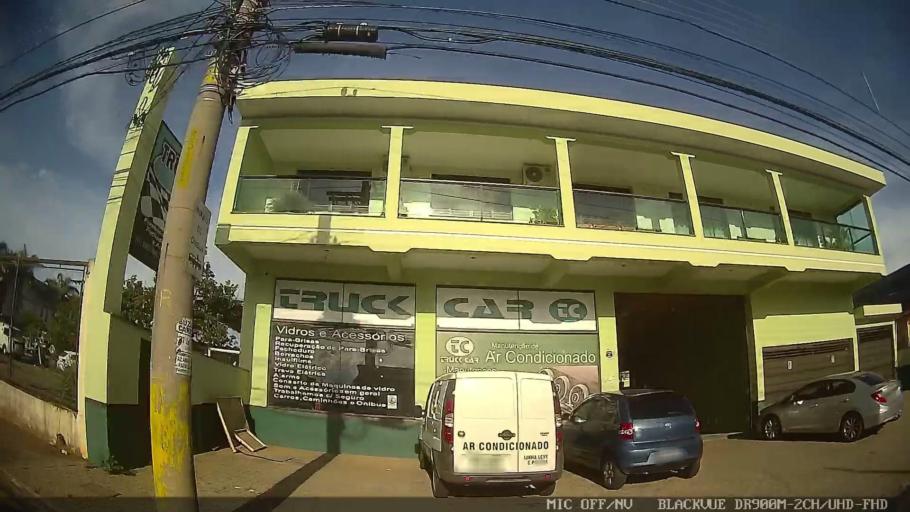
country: BR
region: Sao Paulo
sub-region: Tiete
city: Tiete
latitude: -23.0879
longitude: -47.7181
